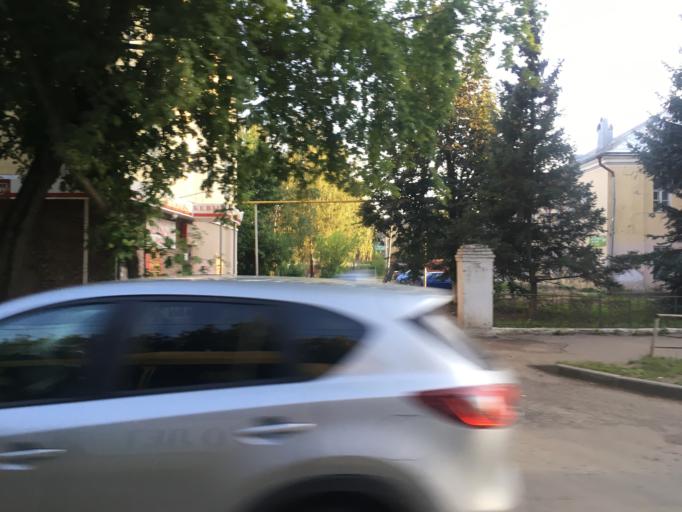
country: RU
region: Mariy-El
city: Yoshkar-Ola
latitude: 56.6459
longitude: 47.8910
